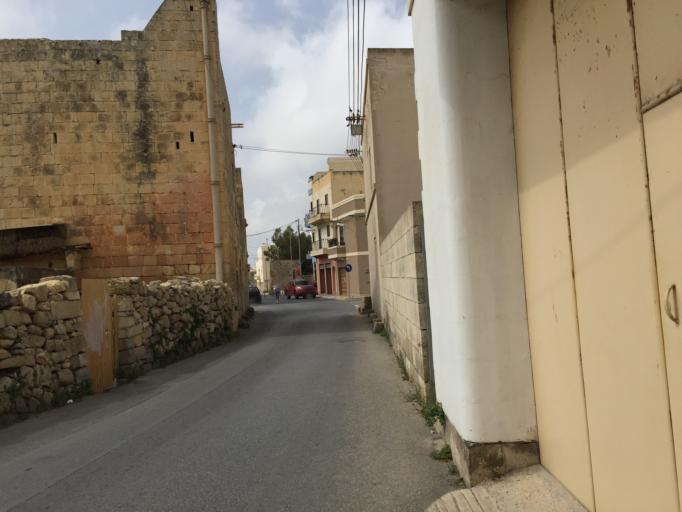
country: MT
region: Haz-Zabbar
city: Zabbar
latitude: 35.8719
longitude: 14.5376
